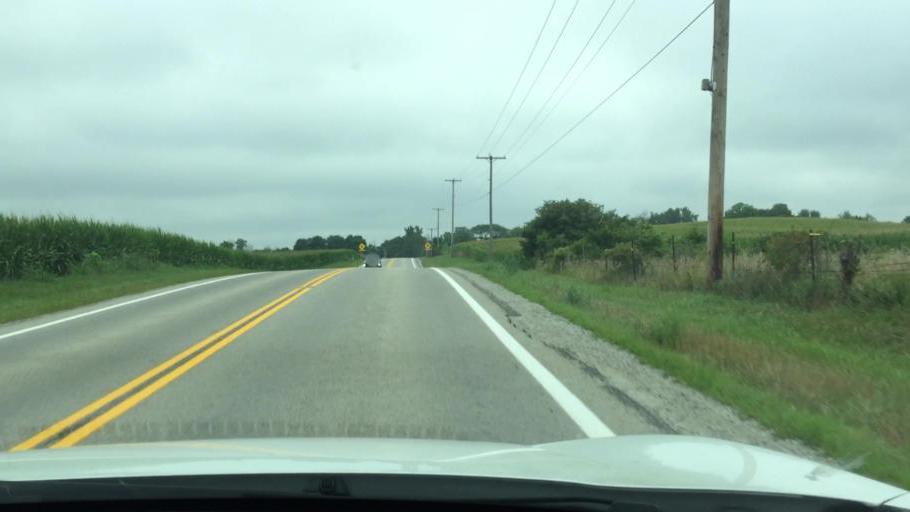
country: US
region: Ohio
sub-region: Clark County
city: Lisbon
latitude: 39.9416
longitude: -83.6115
